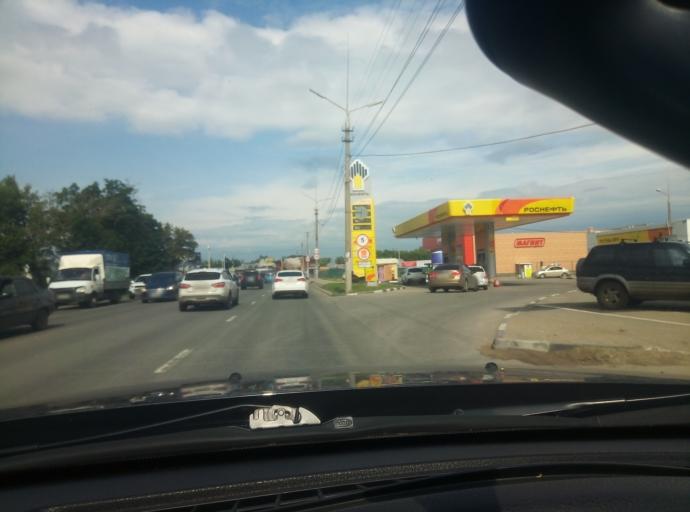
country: RU
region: Tula
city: Tula
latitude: 54.2079
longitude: 37.5760
